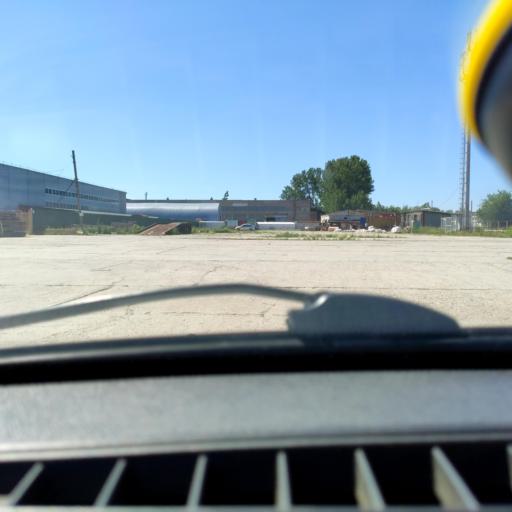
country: RU
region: Samara
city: Tol'yatti
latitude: 53.5728
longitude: 49.3024
